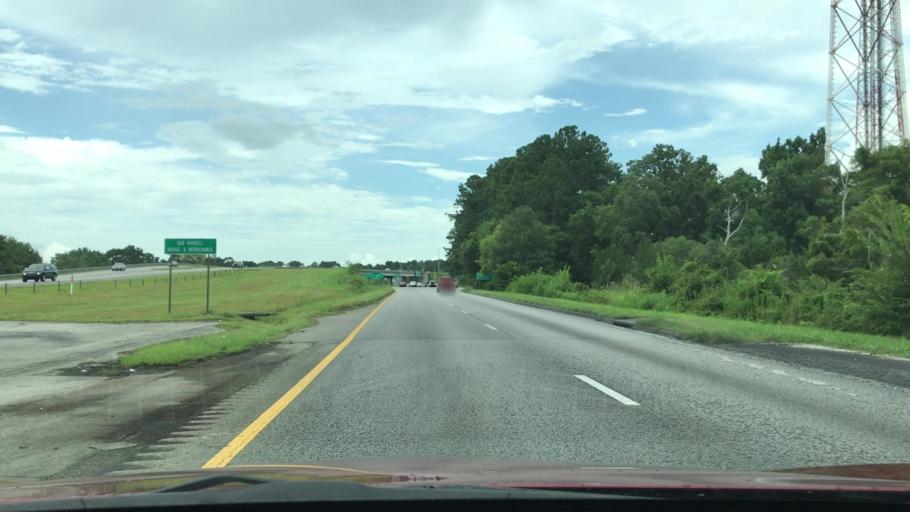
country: US
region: South Carolina
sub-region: Charleston County
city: Shell Point
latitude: 32.7943
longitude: -80.0339
